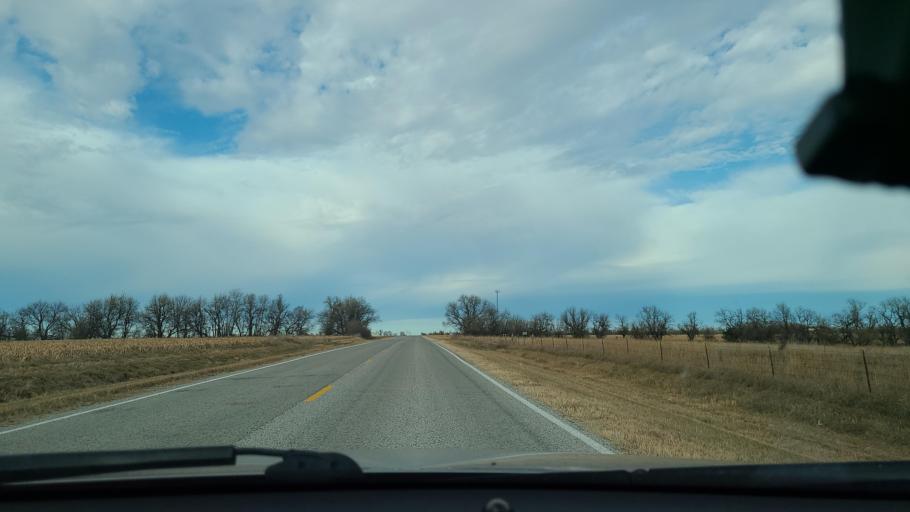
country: US
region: Kansas
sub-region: McPherson County
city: Inman
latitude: 38.3536
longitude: -97.9244
